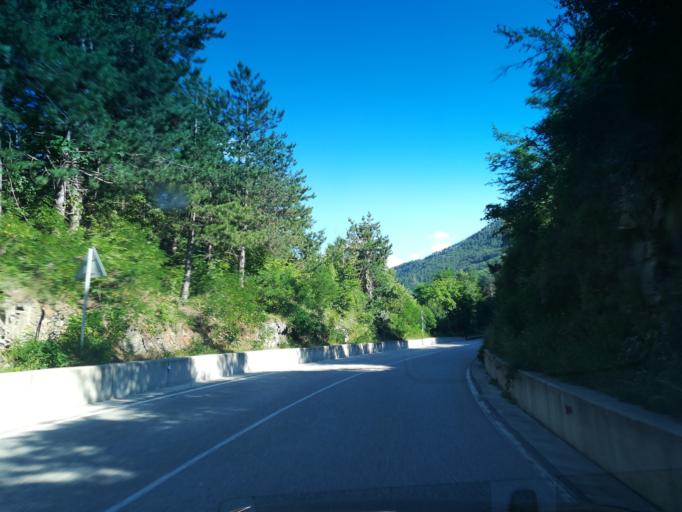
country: BG
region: Smolyan
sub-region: Obshtina Chepelare
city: Chepelare
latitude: 41.8355
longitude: 24.6832
